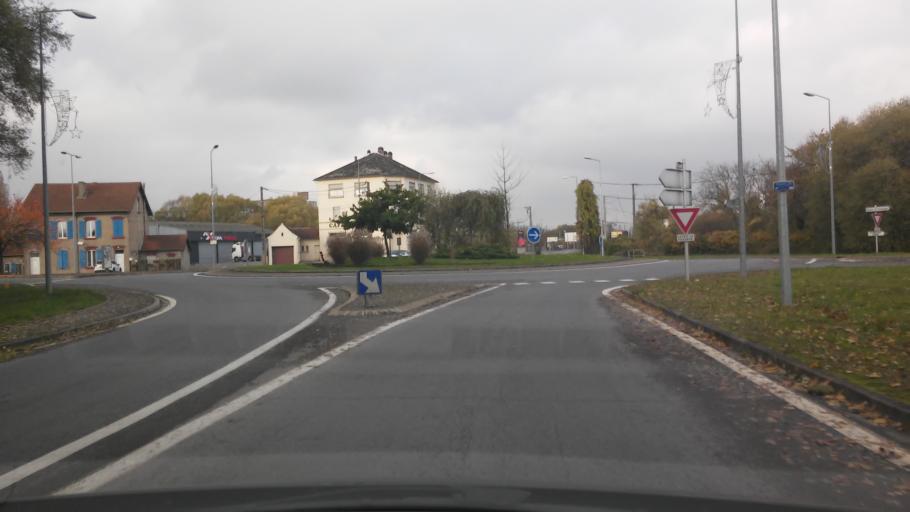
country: FR
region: Lorraine
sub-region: Departement de la Moselle
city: Uckange
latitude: 49.3268
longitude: 6.1529
